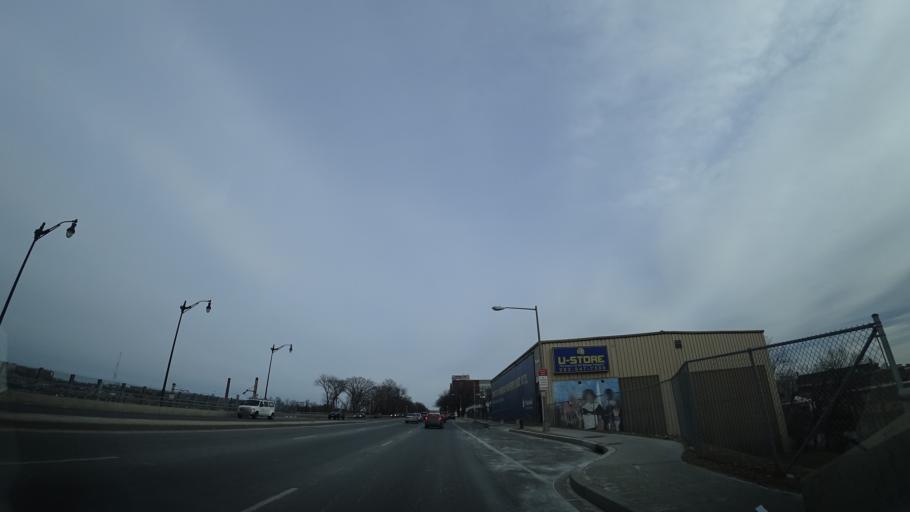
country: US
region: Washington, D.C.
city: Washington, D.C.
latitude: 38.9102
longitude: -77.0006
